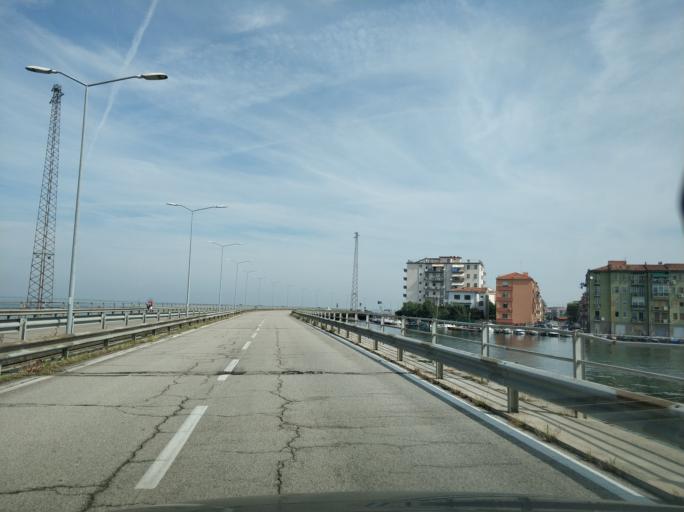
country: IT
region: Veneto
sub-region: Provincia di Venezia
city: Chioggia
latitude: 45.2138
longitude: 12.2728
